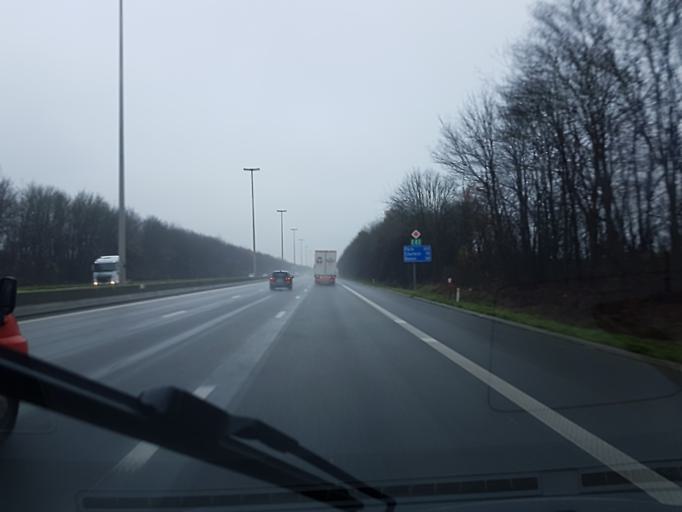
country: BE
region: Wallonia
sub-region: Province de Liege
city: Wanze
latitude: 50.5764
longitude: 5.2010
